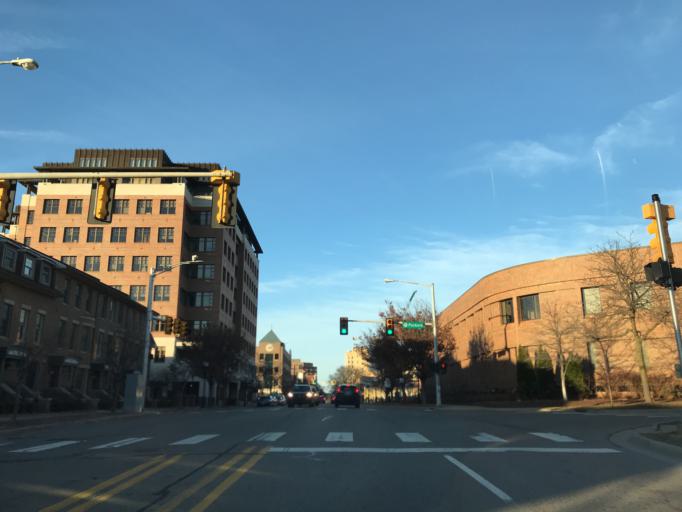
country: US
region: Michigan
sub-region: Washtenaw County
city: Ann Arbor
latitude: 42.2764
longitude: -83.7488
